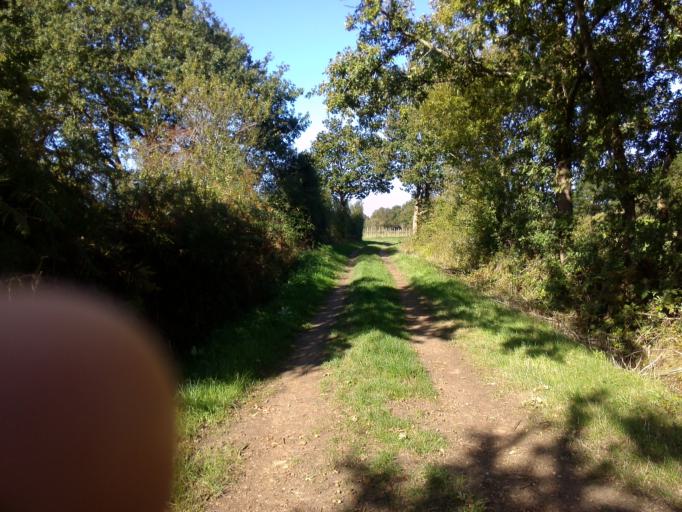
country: FR
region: Pays de la Loire
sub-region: Departement de la Loire-Atlantique
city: Chemere
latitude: 47.1123
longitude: -1.9290
